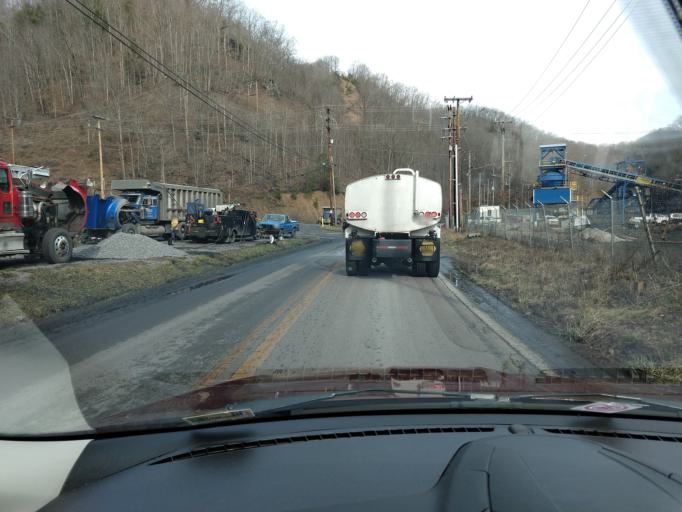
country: US
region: West Virginia
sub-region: McDowell County
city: Welch
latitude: 37.3321
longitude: -81.6841
